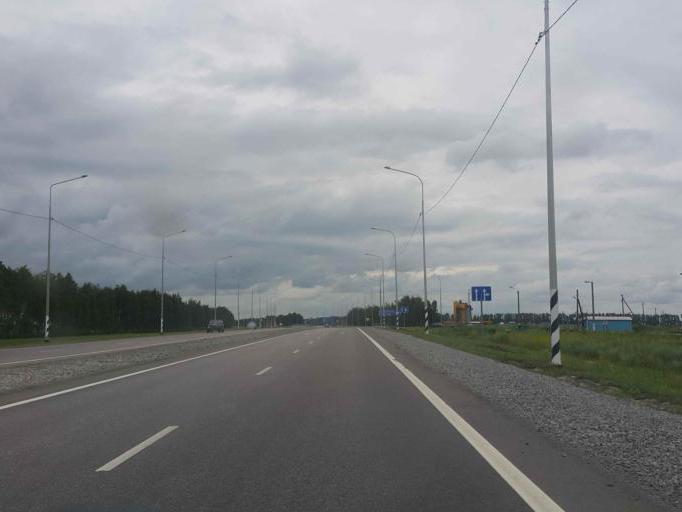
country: RU
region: Tambov
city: Zavoronezhskoye
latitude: 52.8624
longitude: 40.7655
